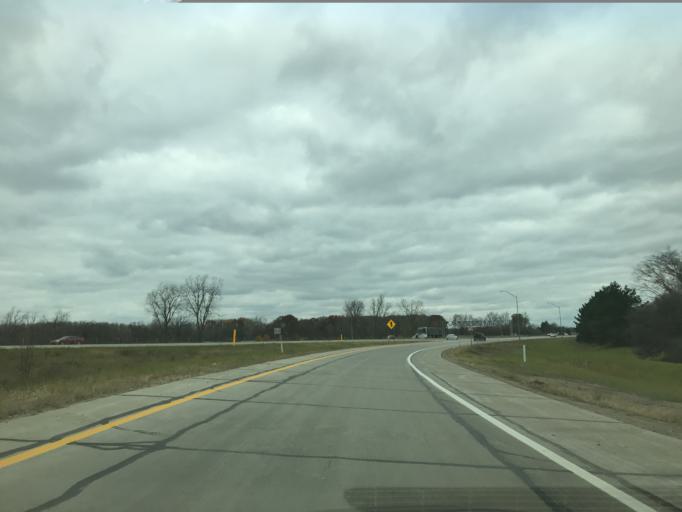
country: US
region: Michigan
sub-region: Eaton County
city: Waverly
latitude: 42.7434
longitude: -84.6669
